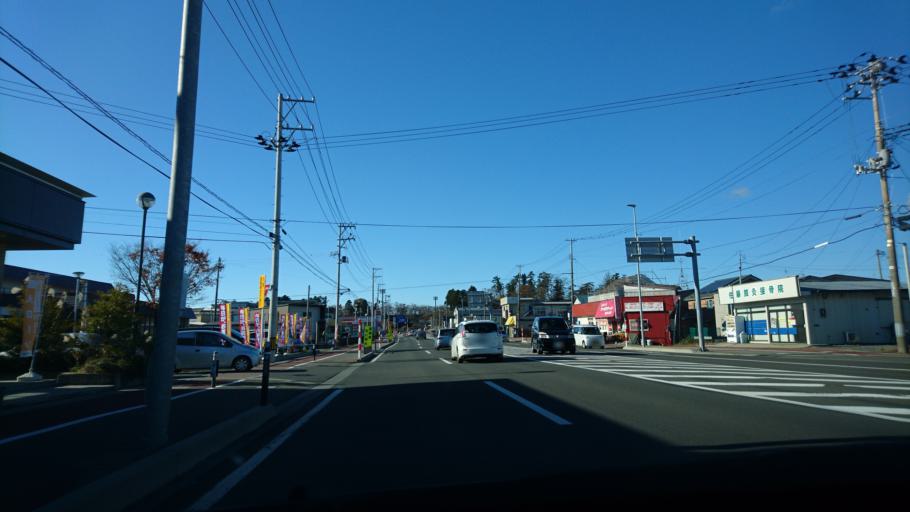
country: JP
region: Akita
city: Akita Shi
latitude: 39.3817
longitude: 140.0514
